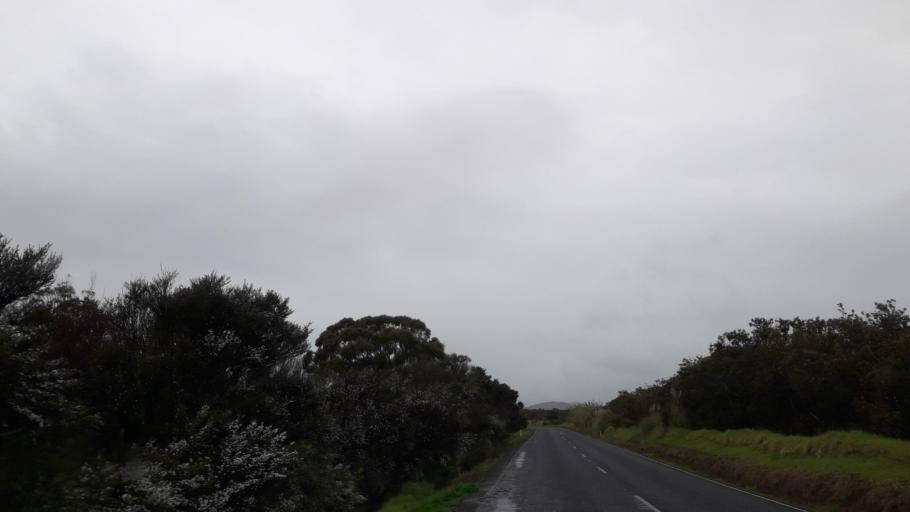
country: NZ
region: Northland
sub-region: Far North District
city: Kaitaia
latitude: -35.3718
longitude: 173.5023
